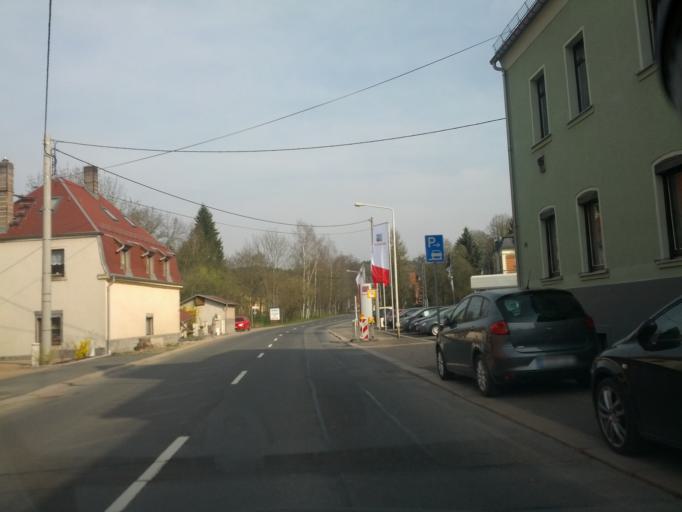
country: DE
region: Saxony
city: Kirchberg
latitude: 50.6171
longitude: 12.5331
